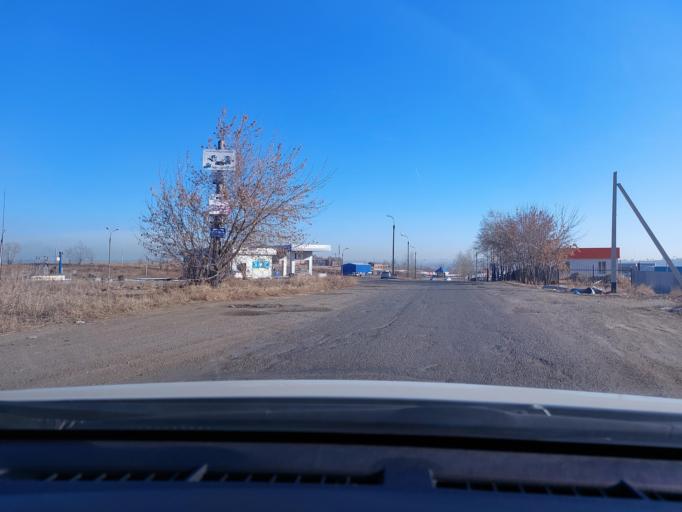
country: RU
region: Irkutsk
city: Smolenshchina
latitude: 52.3239
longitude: 104.1858
